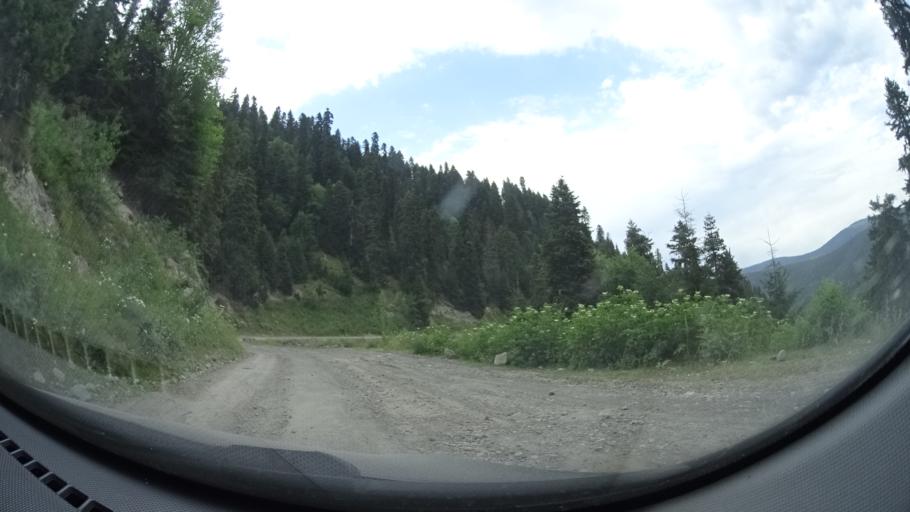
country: GE
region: Samtskhe-Javakheti
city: Adigeni
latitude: 41.6363
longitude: 42.5795
